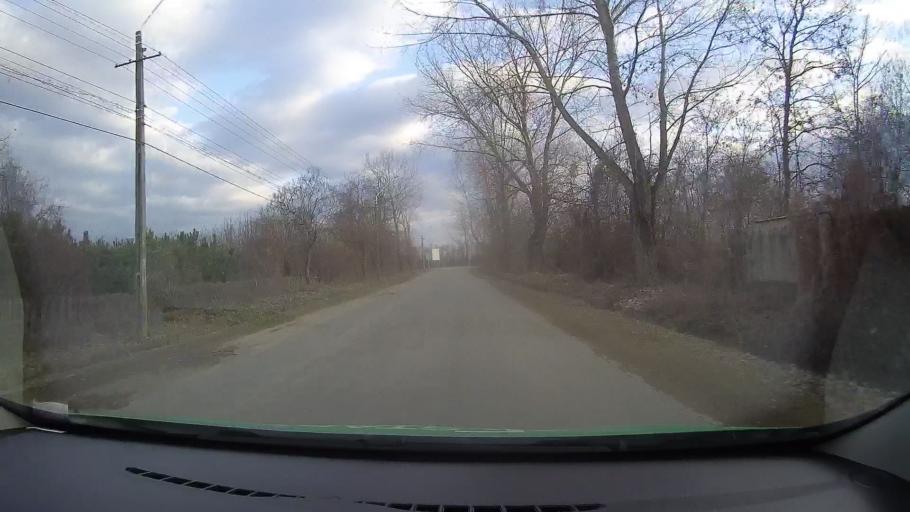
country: RO
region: Dambovita
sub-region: Municipiul Moreni
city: Moreni
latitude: 44.9630
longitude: 25.6564
